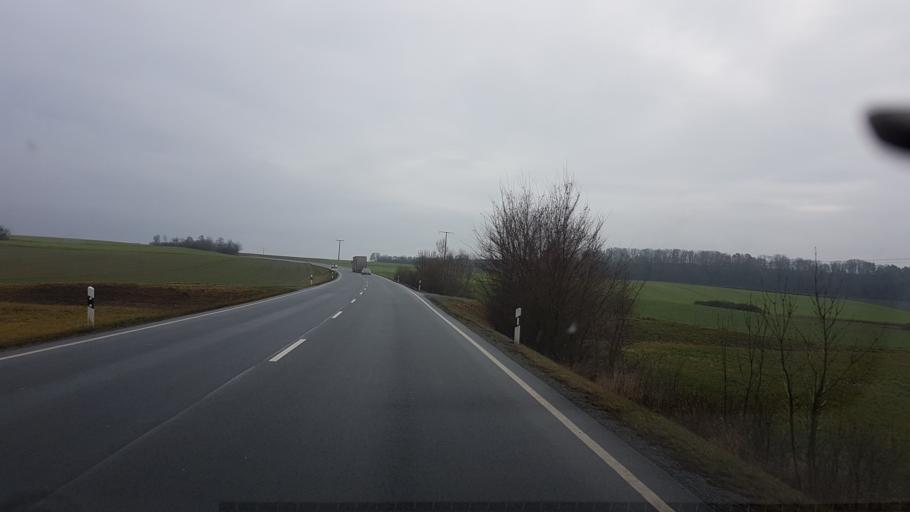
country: DE
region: Bavaria
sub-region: Regierungsbezirk Unterfranken
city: Bad Konigshofen im Grabfeld
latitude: 50.2822
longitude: 10.4911
